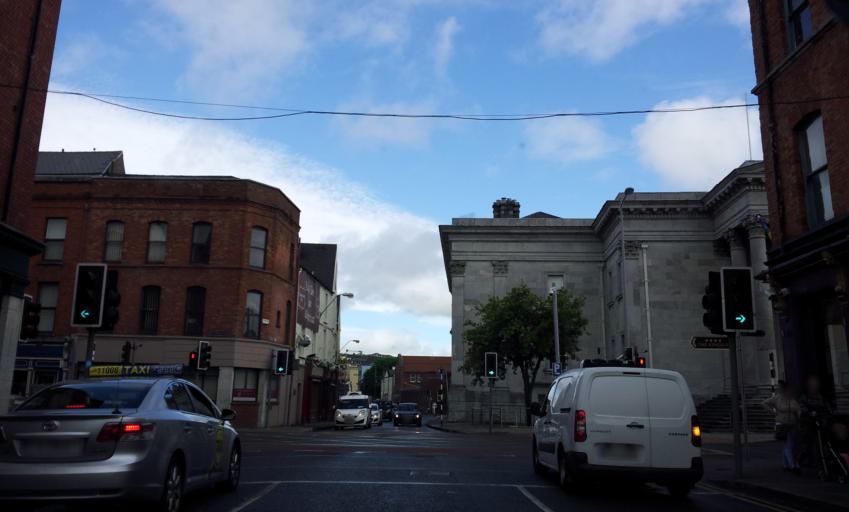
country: IE
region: Munster
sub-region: County Cork
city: Cork
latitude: 51.8972
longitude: -8.4790
